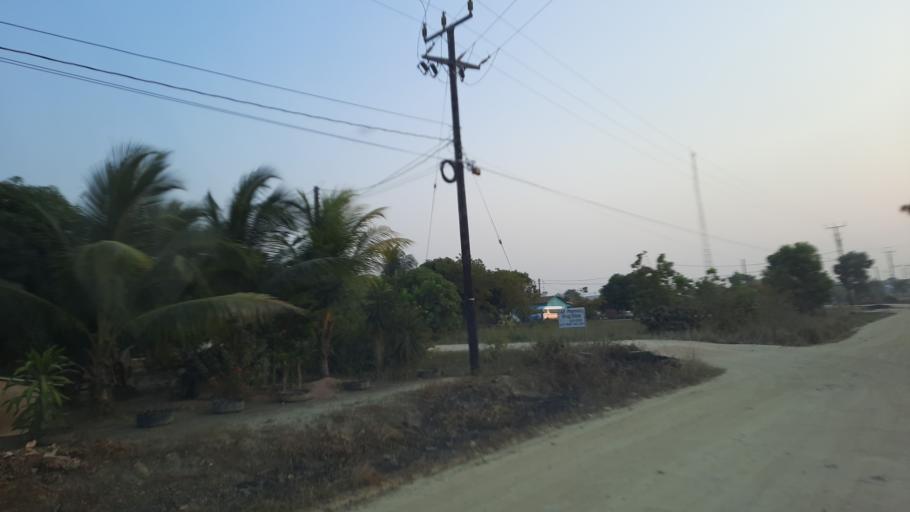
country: BZ
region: Stann Creek
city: Placencia
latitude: 16.5333
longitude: -88.4281
